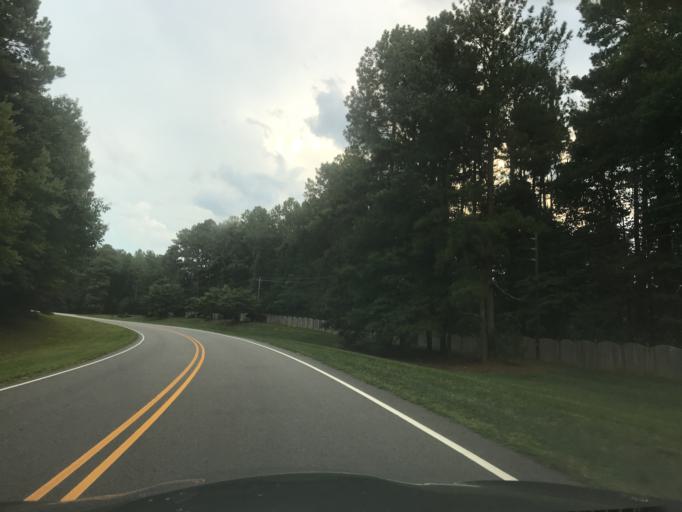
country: US
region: North Carolina
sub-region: Wake County
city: Wake Forest
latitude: 35.9216
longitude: -78.6025
